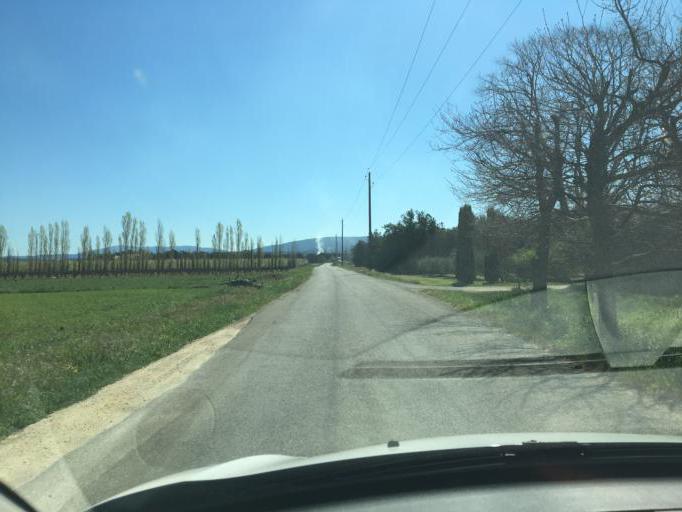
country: FR
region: Provence-Alpes-Cote d'Azur
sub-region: Departement du Vaucluse
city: Robion
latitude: 43.8640
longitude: 5.1250
